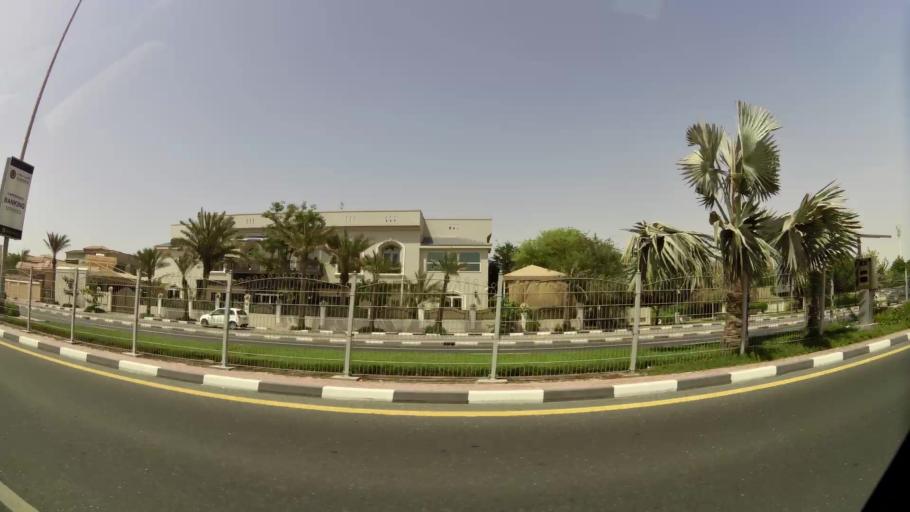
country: AE
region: Dubai
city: Dubai
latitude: 25.1513
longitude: 55.2209
